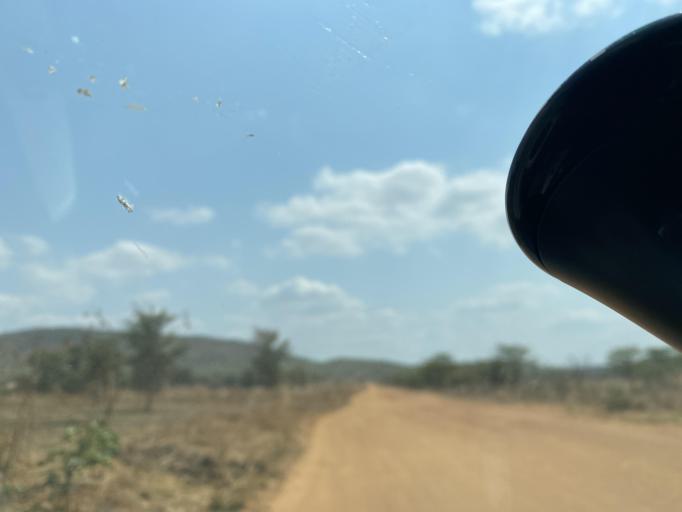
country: ZM
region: Lusaka
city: Chongwe
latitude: -15.5989
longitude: 28.7522
